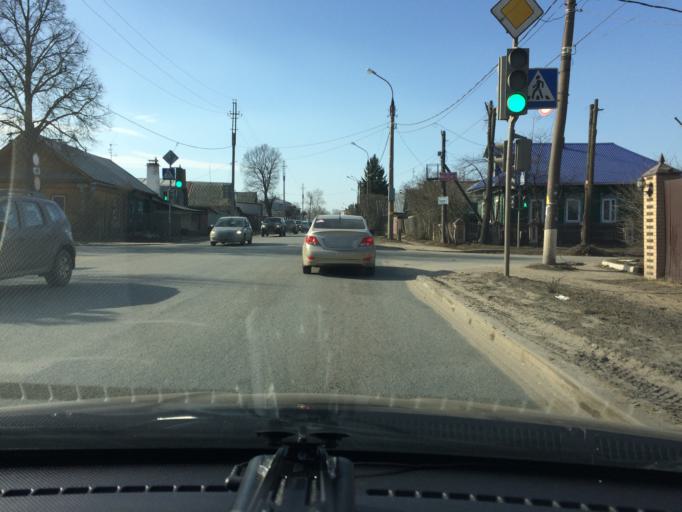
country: RU
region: Mariy-El
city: Yoshkar-Ola
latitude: 56.6463
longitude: 47.9070
